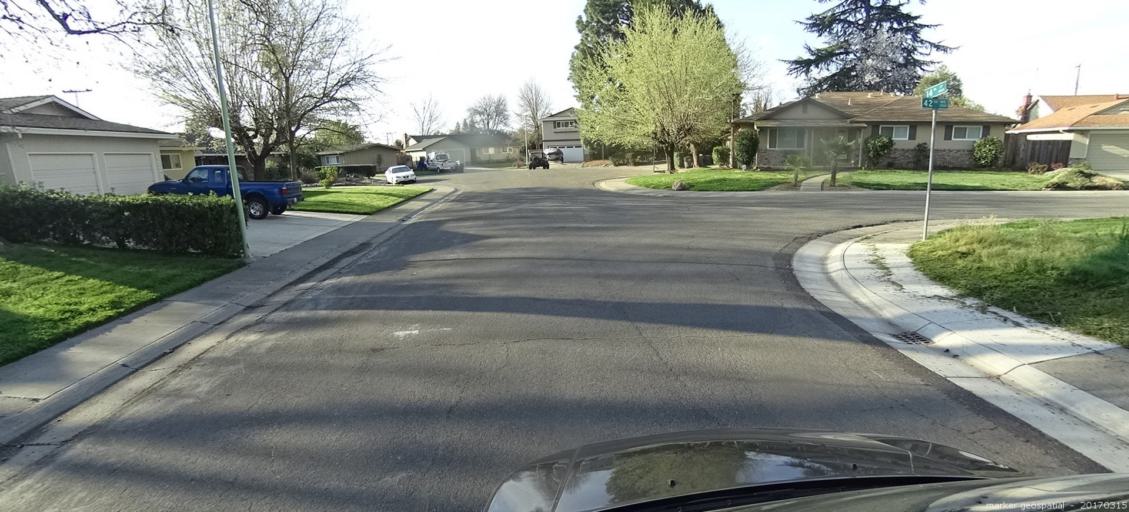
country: US
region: California
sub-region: Sacramento County
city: Parkway
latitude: 38.5148
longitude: -121.5070
